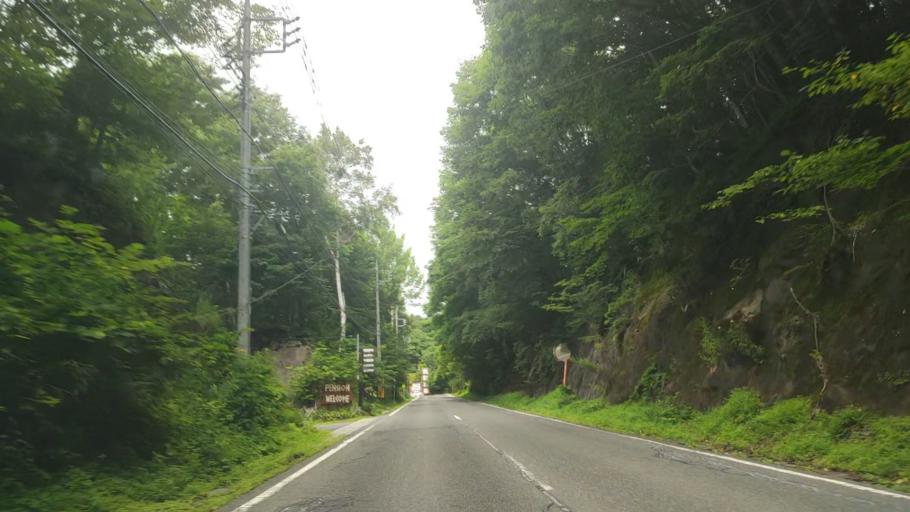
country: JP
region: Tochigi
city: Nikko
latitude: 36.8141
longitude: 139.3288
